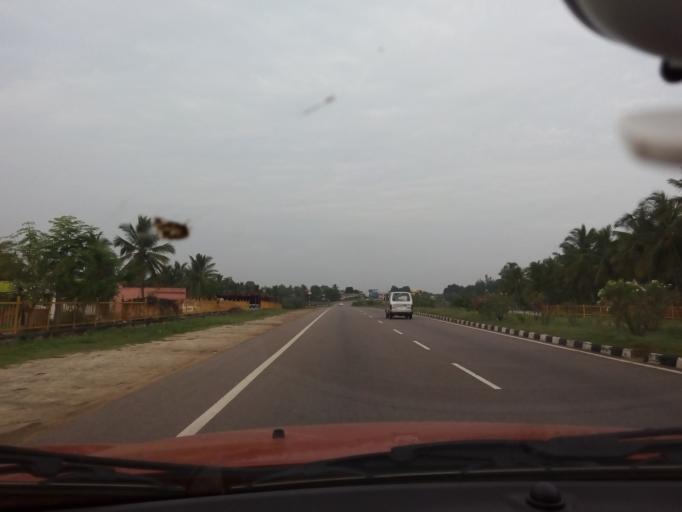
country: IN
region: Karnataka
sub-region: Tumkur
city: Kunigal
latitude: 12.9973
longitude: 76.9361
